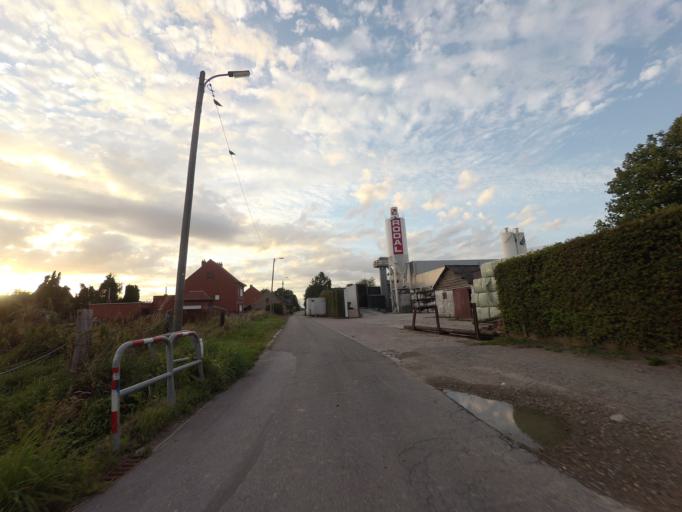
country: BE
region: Flanders
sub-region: Provincie Vlaams-Brabant
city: Kapelle-op-den-Bos
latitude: 50.9764
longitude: 4.3477
